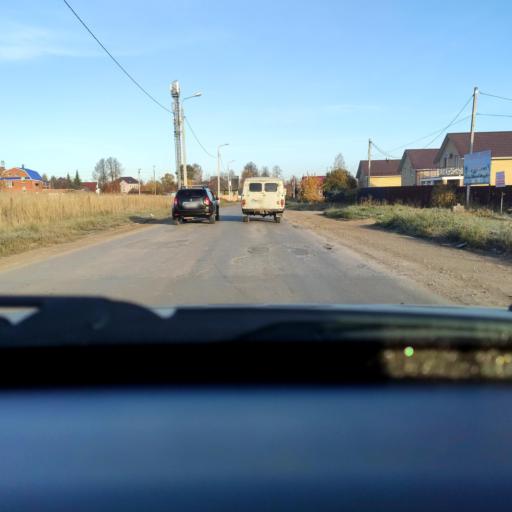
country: RU
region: Perm
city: Perm
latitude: 58.0204
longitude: 56.3360
